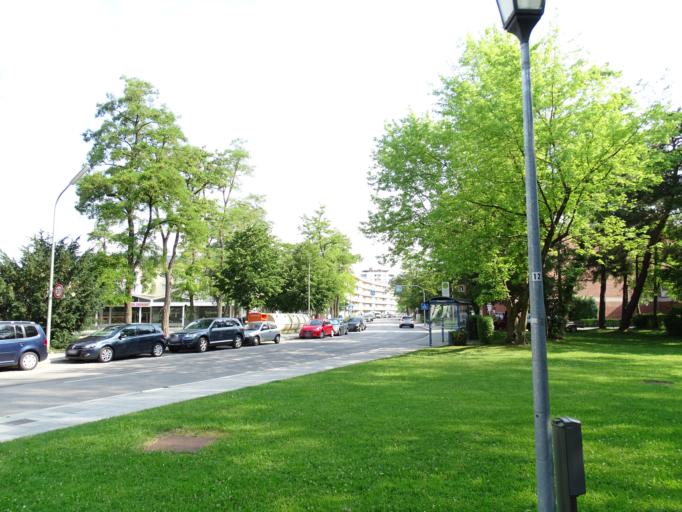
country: DE
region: Bavaria
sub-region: Upper Bavaria
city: Oberschleissheim
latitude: 48.2166
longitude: 11.5535
